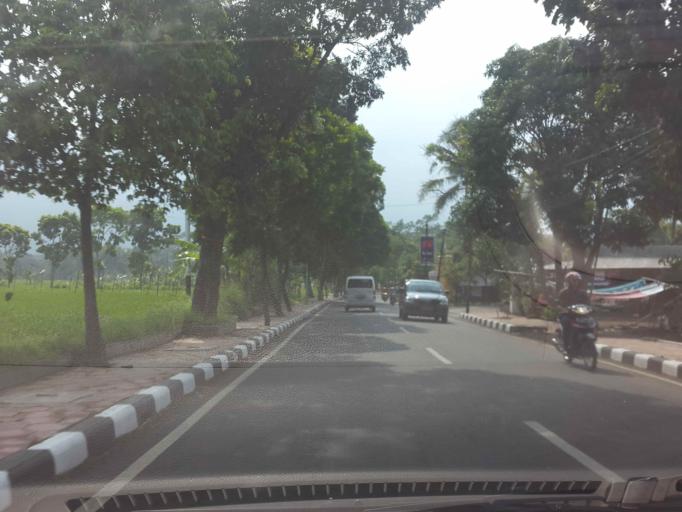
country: ID
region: Central Java
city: Salatiga
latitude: -7.3193
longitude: 110.4839
